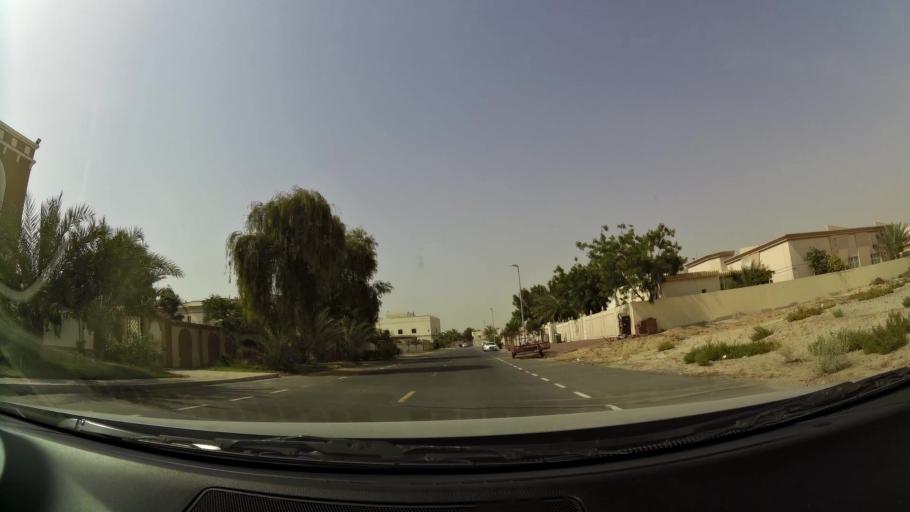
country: AE
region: Ash Shariqah
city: Sharjah
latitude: 25.2494
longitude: 55.4398
